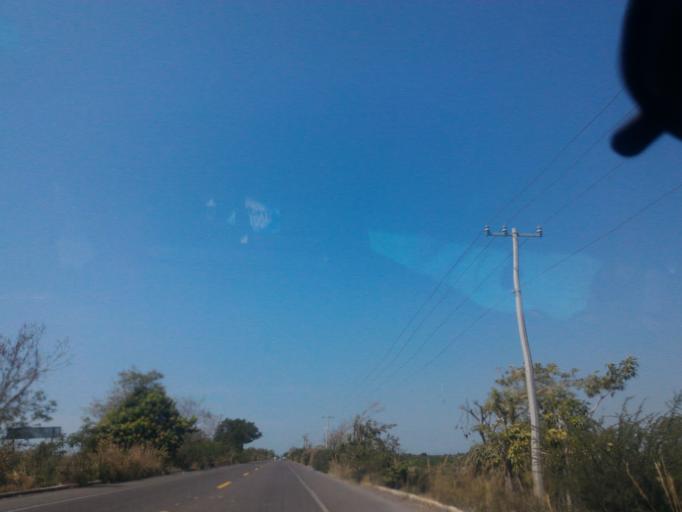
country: MX
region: Michoacan
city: Coahuayana Viejo
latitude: 18.7756
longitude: -103.7507
